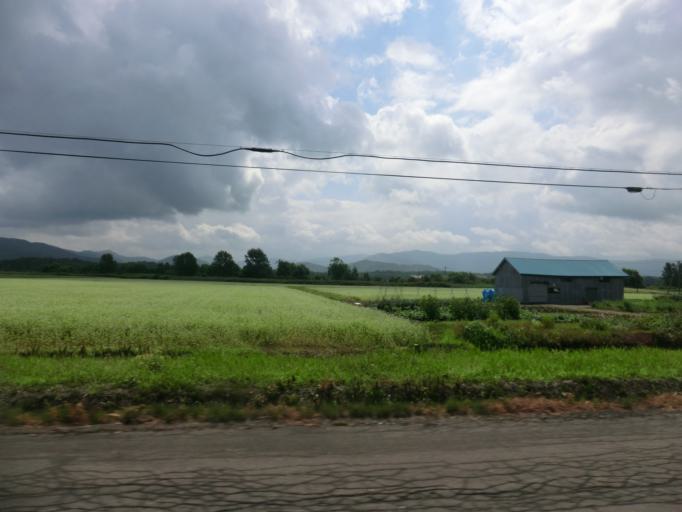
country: JP
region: Hokkaido
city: Fukagawa
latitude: 44.0014
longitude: 142.1455
